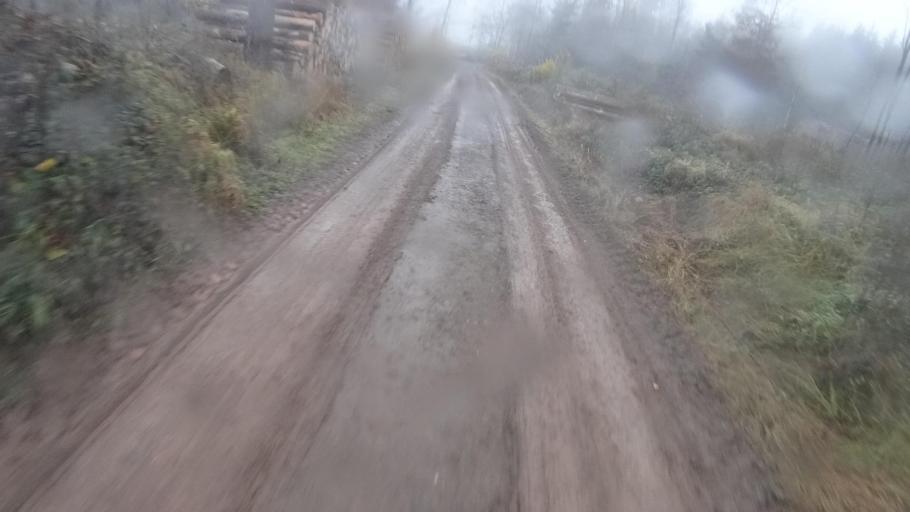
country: DE
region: Rheinland-Pfalz
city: Karbach
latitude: 50.1659
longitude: 7.6026
